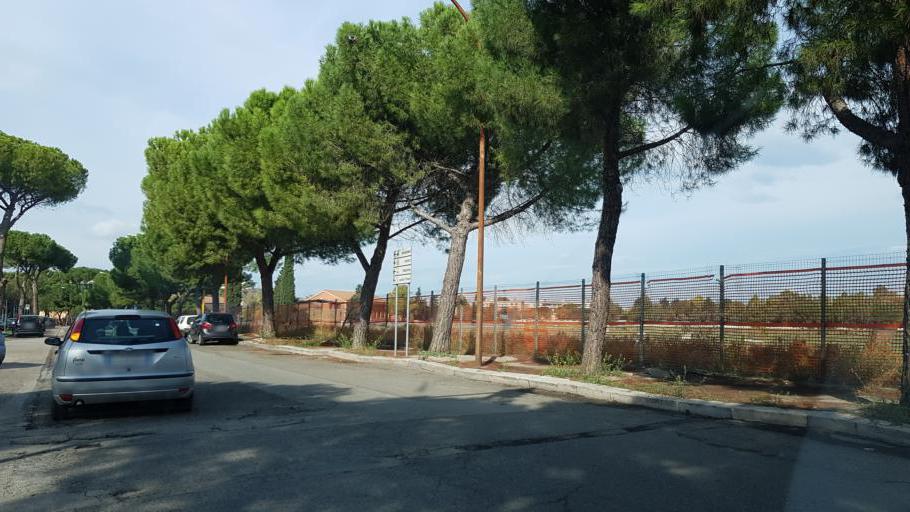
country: IT
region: Apulia
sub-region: Provincia di Foggia
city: Foggia
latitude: 41.4572
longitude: 15.5607
